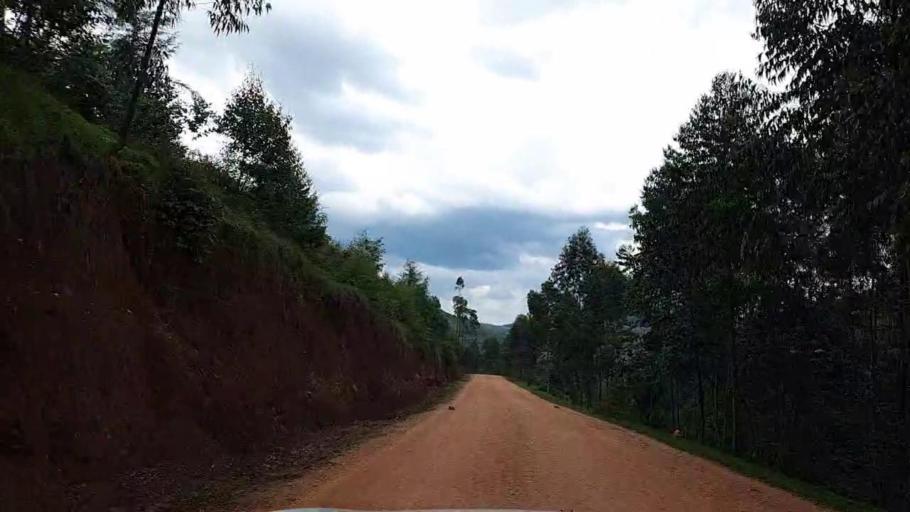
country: RW
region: Southern Province
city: Nyanza
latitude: -2.4040
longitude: 29.6763
